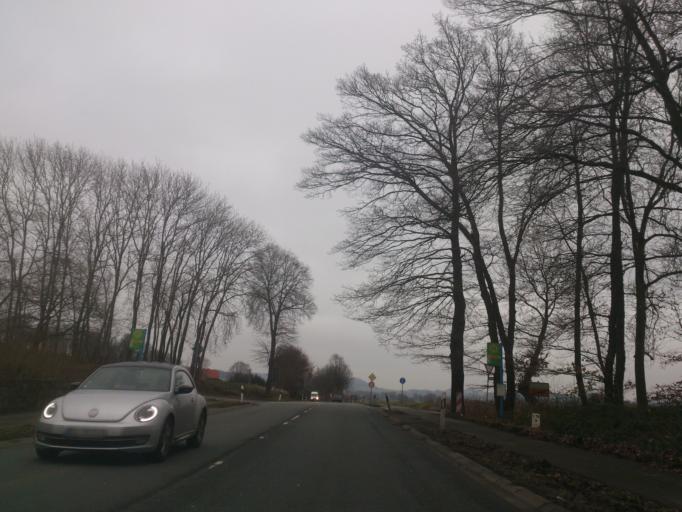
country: DE
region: North Rhine-Westphalia
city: Bad Oeynhausen
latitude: 52.1416
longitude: 8.7847
